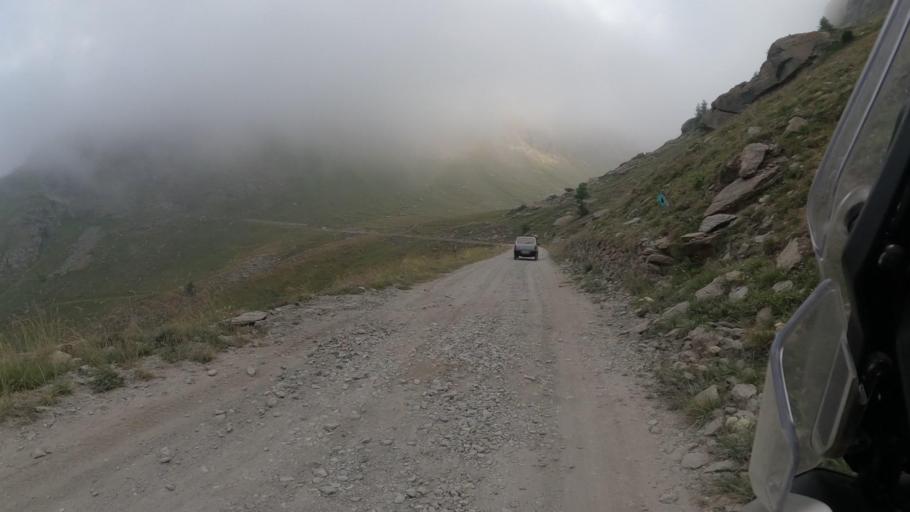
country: IT
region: Piedmont
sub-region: Provincia di Torino
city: Usseaux
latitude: 45.0621
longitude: 6.9763
